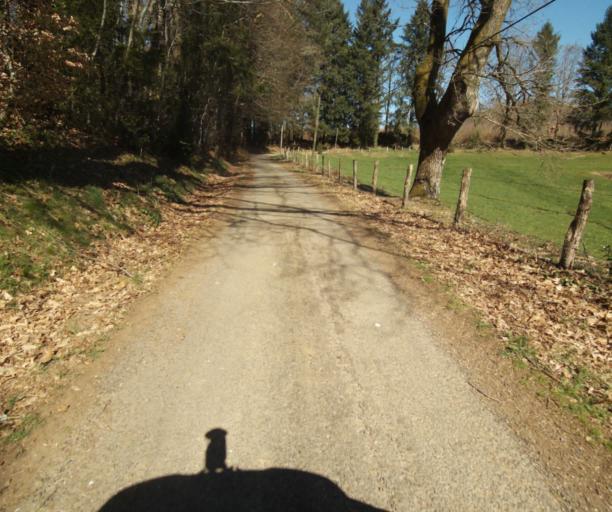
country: FR
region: Limousin
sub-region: Departement de la Correze
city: Saint-Clement
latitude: 45.3555
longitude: 1.6531
